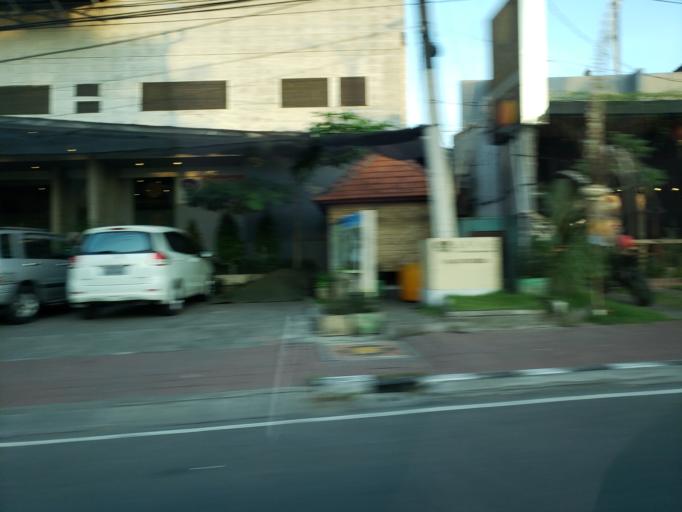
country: ID
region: Bali
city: Jimbaran
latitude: -8.7884
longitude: 115.1773
